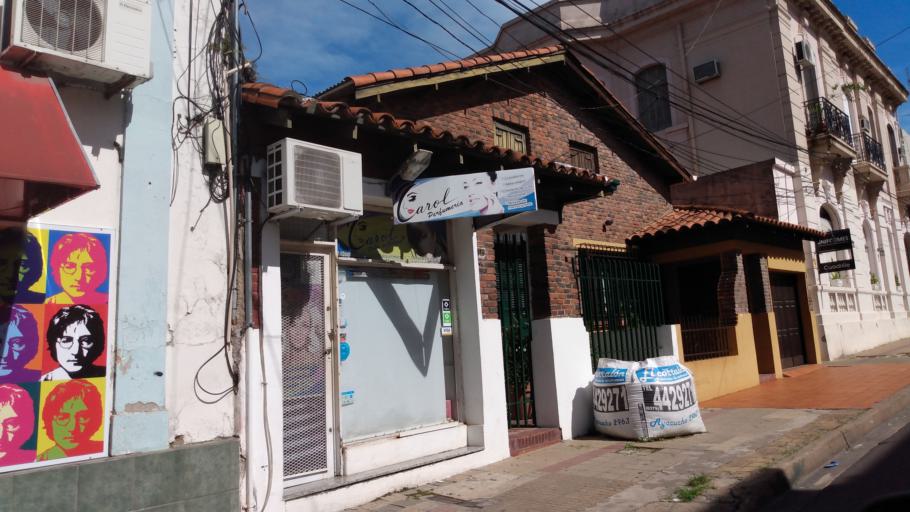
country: AR
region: Corrientes
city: Corrientes
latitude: -27.4639
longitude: -58.8339
